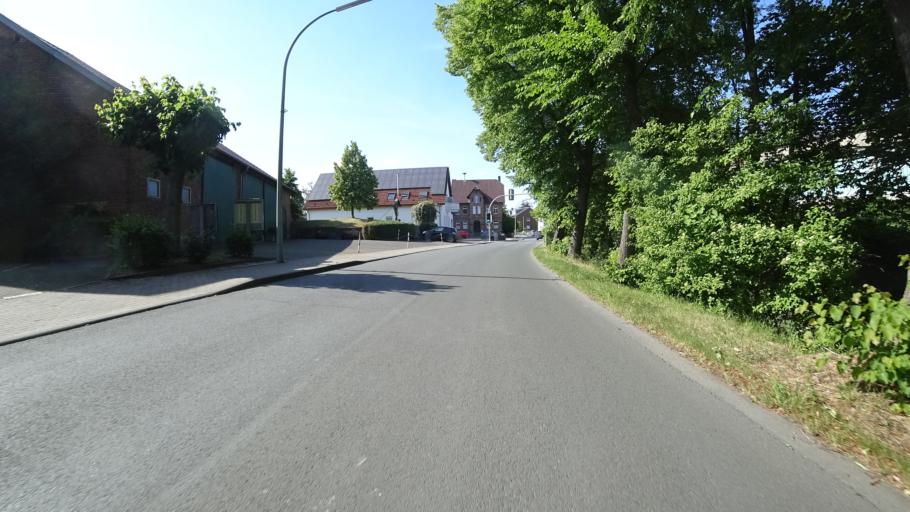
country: DE
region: North Rhine-Westphalia
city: Erwitte
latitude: 51.6285
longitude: 8.3640
